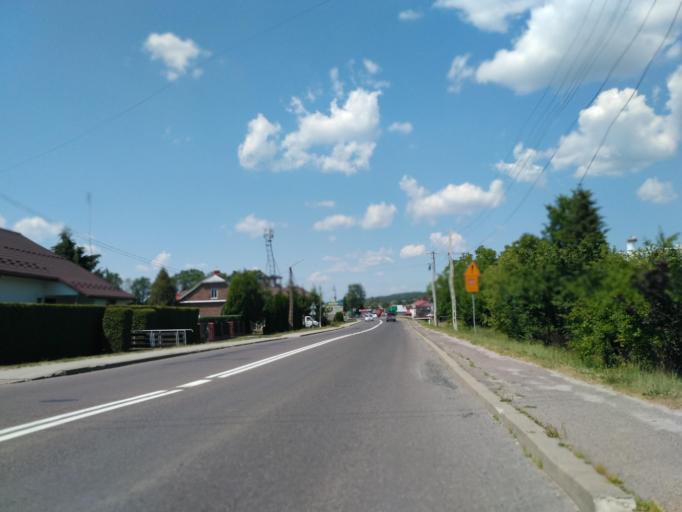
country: PL
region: Subcarpathian Voivodeship
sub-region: Powiat brzozowski
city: Grabownica Starzenska
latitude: 49.6557
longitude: 22.0798
